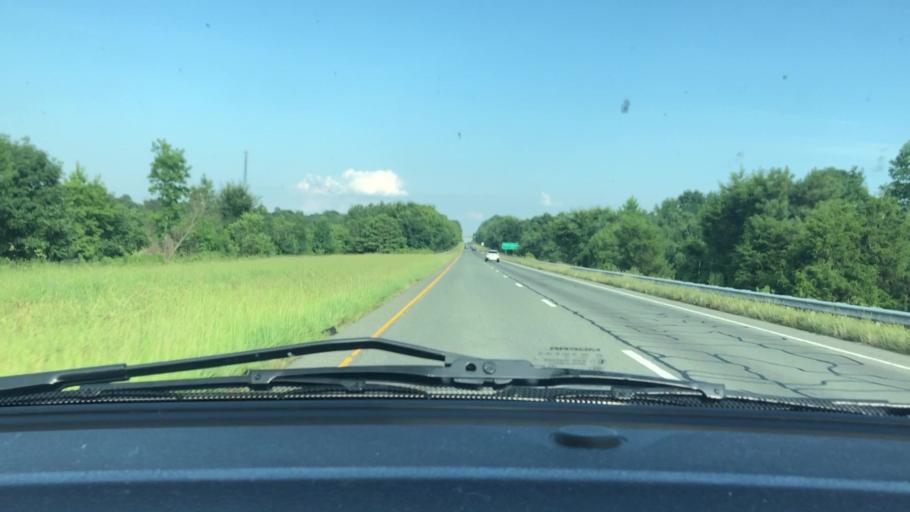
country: US
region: North Carolina
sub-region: Chatham County
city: Siler City
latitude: 35.7817
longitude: -79.5120
